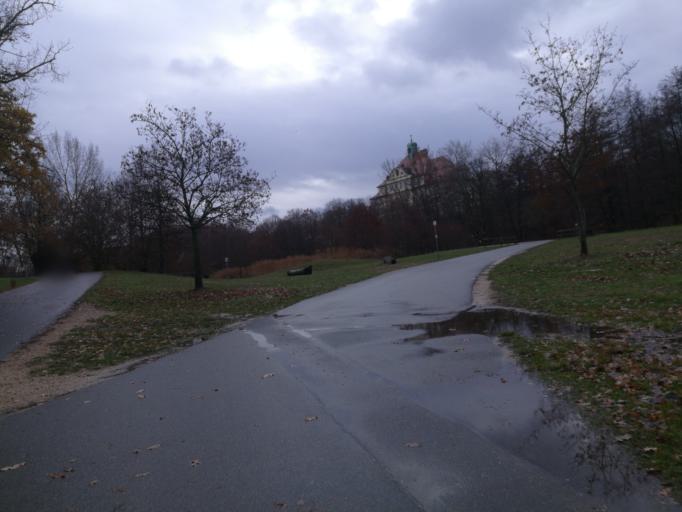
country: DE
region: Bavaria
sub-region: Regierungsbezirk Mittelfranken
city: Wetzendorf
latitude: 49.4575
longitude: 11.0502
